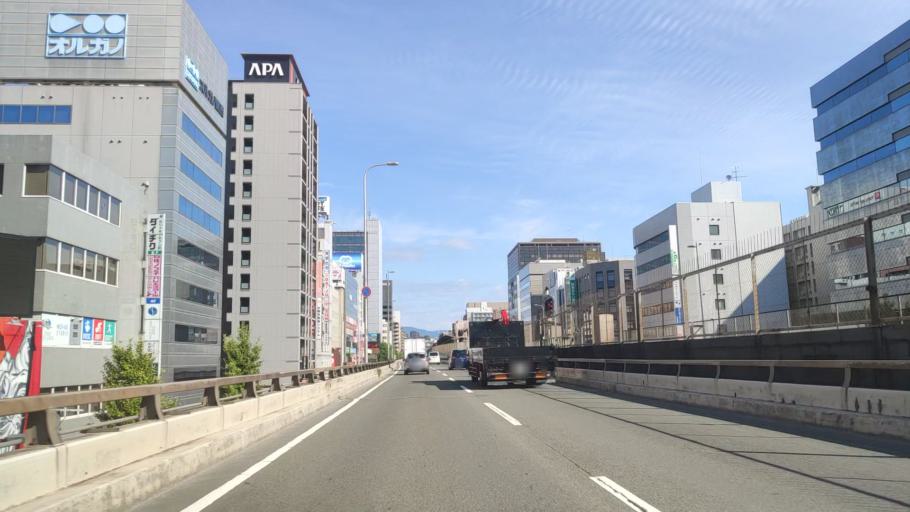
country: JP
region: Osaka
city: Suita
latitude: 34.7562
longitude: 135.4968
